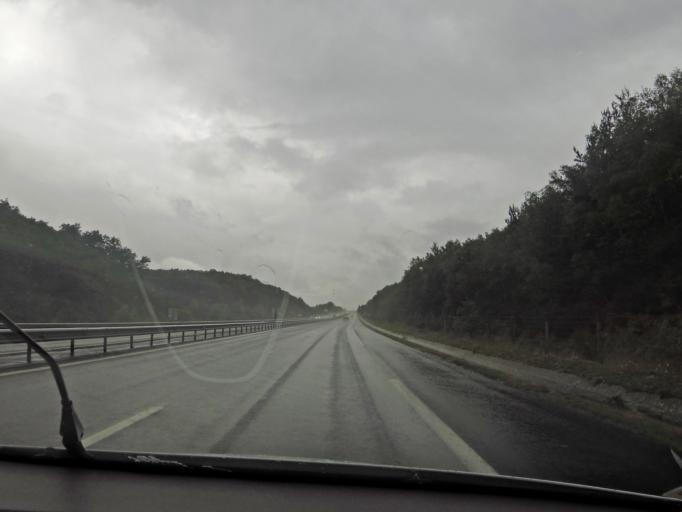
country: FR
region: Auvergne
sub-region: Departement du Cantal
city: Massiac
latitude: 45.1702
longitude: 3.1631
